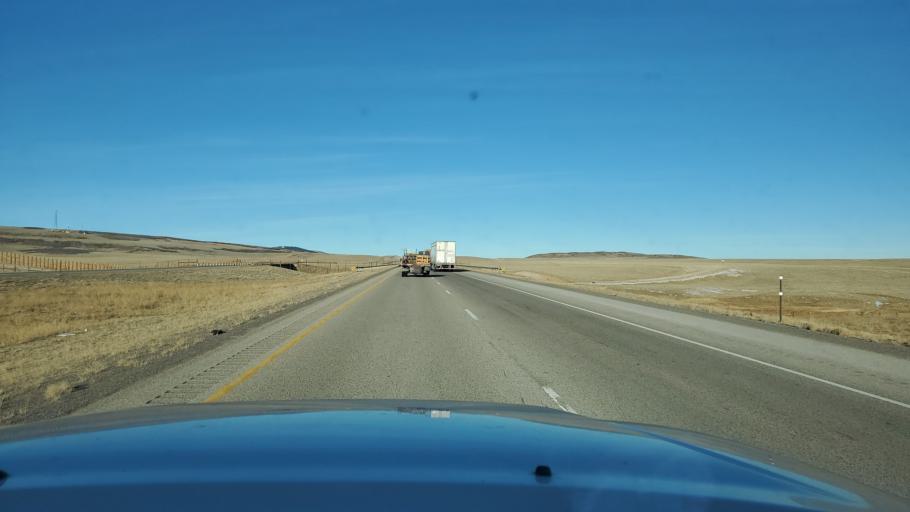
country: US
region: Wyoming
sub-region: Albany County
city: Laramie
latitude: 41.4838
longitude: -106.0230
